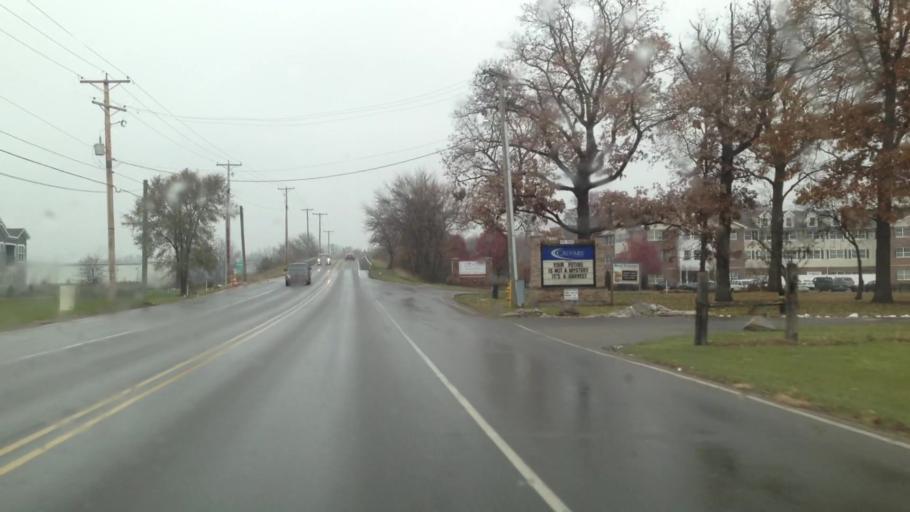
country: US
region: Indiana
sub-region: Saint Joseph County
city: Mishawaka
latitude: 41.7168
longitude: -86.1634
